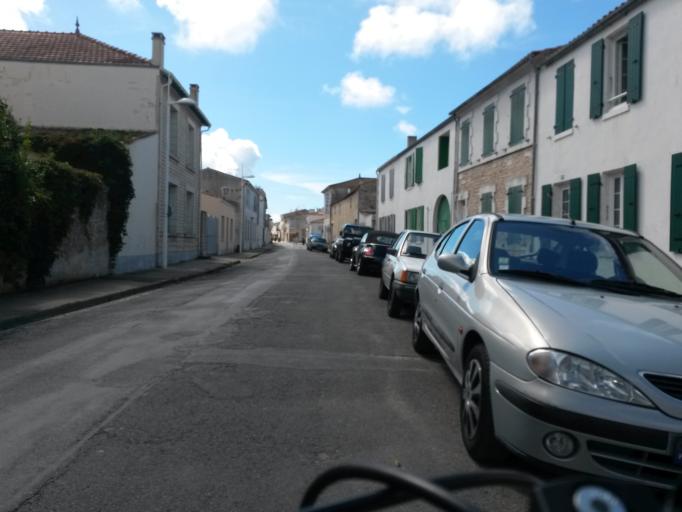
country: FR
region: Poitou-Charentes
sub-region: Departement de la Charente-Maritime
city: Dolus-d'Oleron
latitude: 45.9466
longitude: -1.3042
